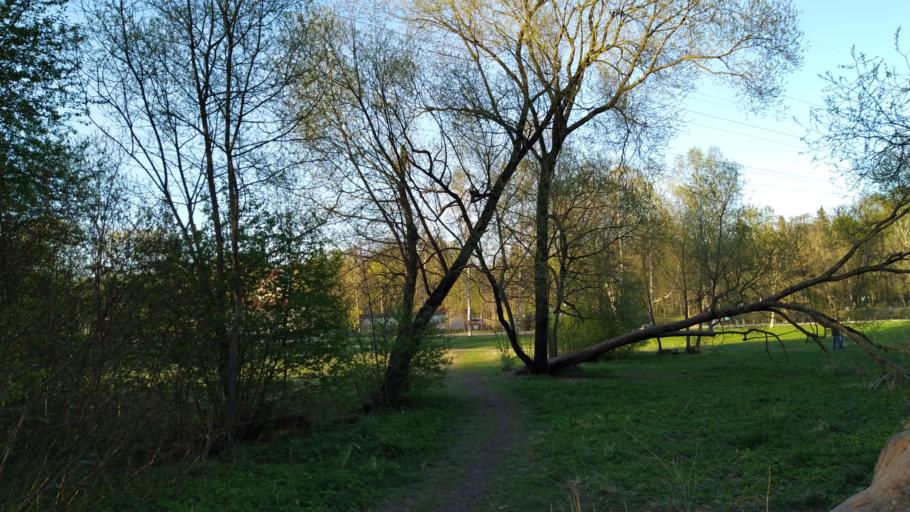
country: RU
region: St.-Petersburg
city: Pushkin
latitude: 59.7112
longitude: 30.4191
